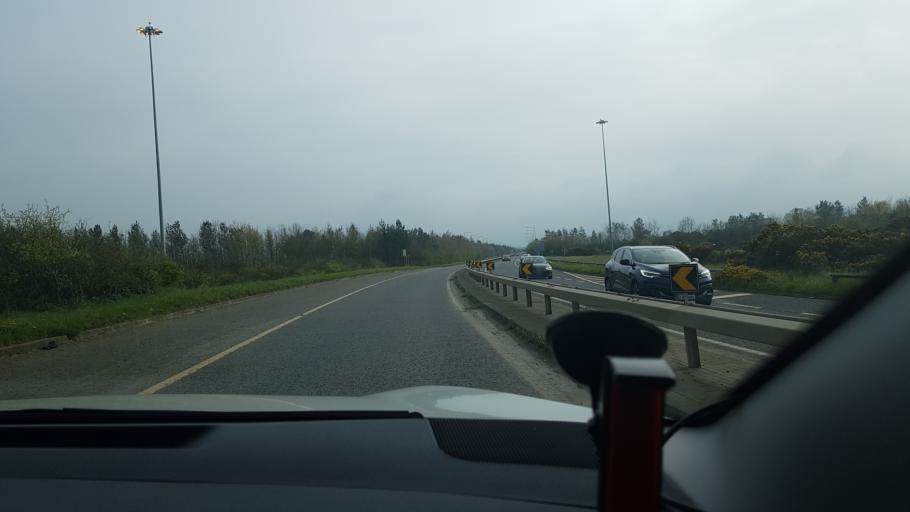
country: IE
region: Leinster
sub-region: An Mhi
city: Stamullin
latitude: 53.6464
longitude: -6.2509
